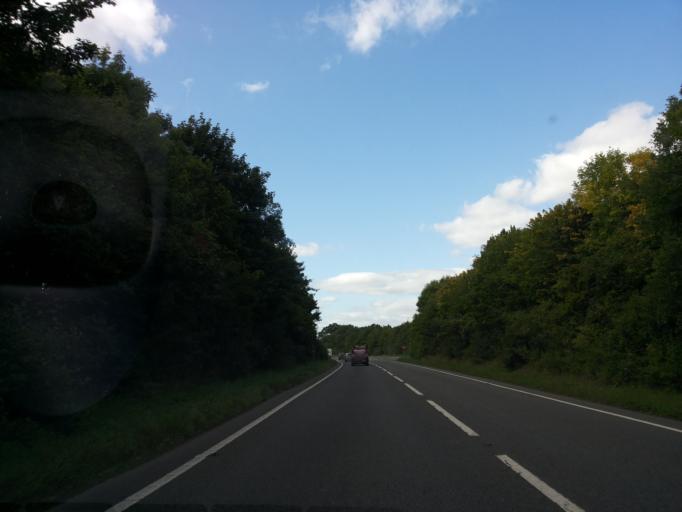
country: GB
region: England
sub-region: Wiltshire
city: Bishopstrow
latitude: 51.1839
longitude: -2.1349
